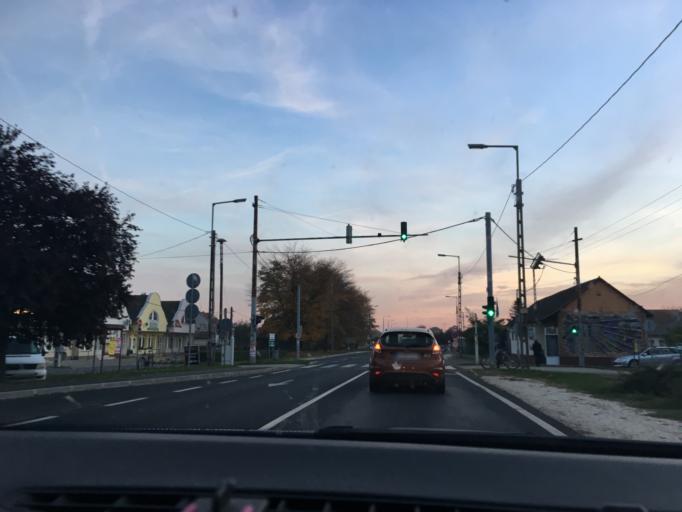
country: HU
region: Hajdu-Bihar
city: Hajduhadhaz
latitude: 47.6438
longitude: 21.6597
